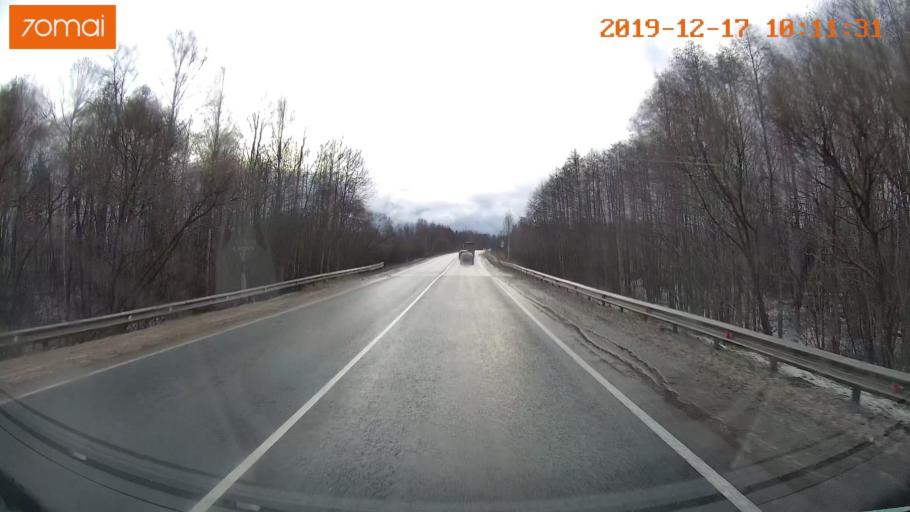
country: RU
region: Vladimir
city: Anopino
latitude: 55.8233
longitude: 40.6574
